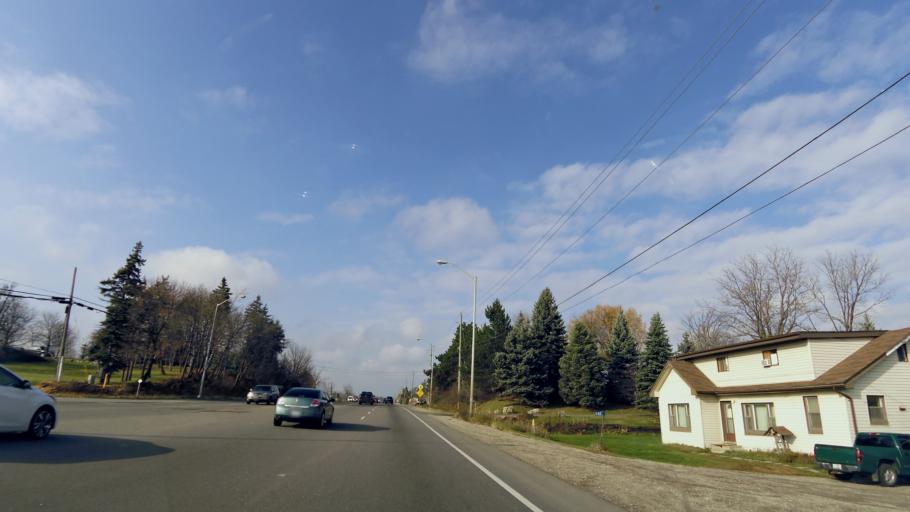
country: CA
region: Ontario
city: Hamilton
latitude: 43.3224
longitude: -79.9315
